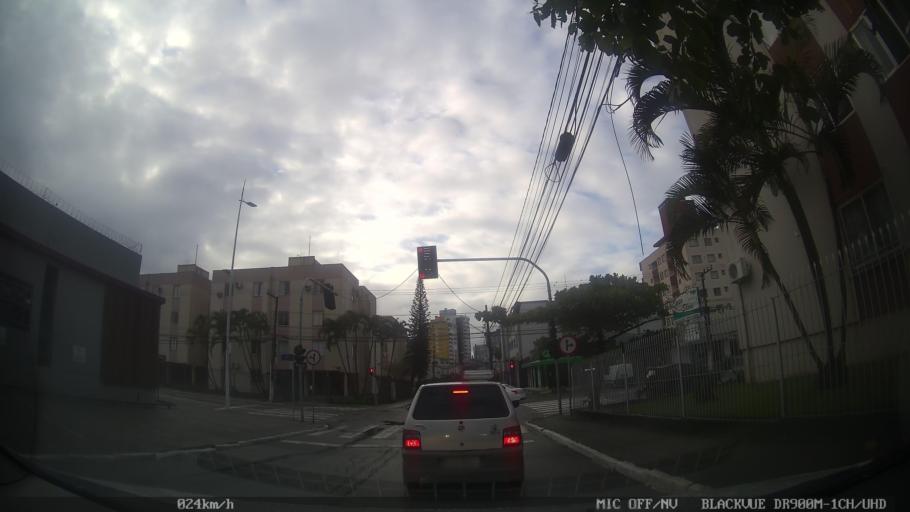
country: BR
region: Santa Catarina
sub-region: Sao Jose
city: Campinas
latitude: -27.5902
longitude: -48.6128
